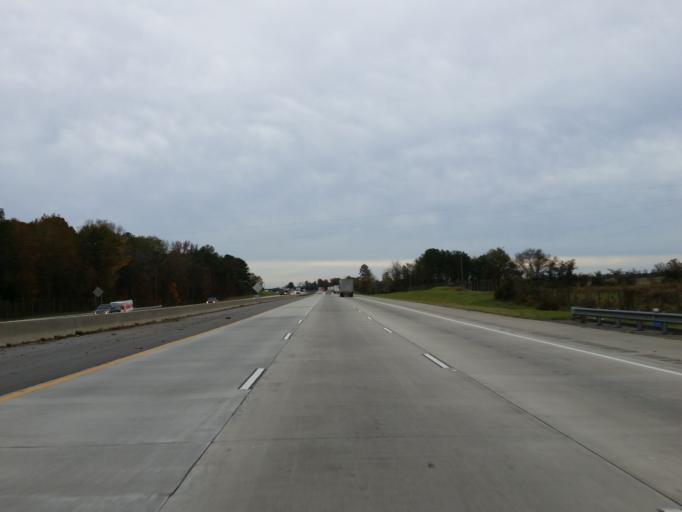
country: US
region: Georgia
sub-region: Dooly County
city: Unadilla
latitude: 32.3017
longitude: -83.7618
